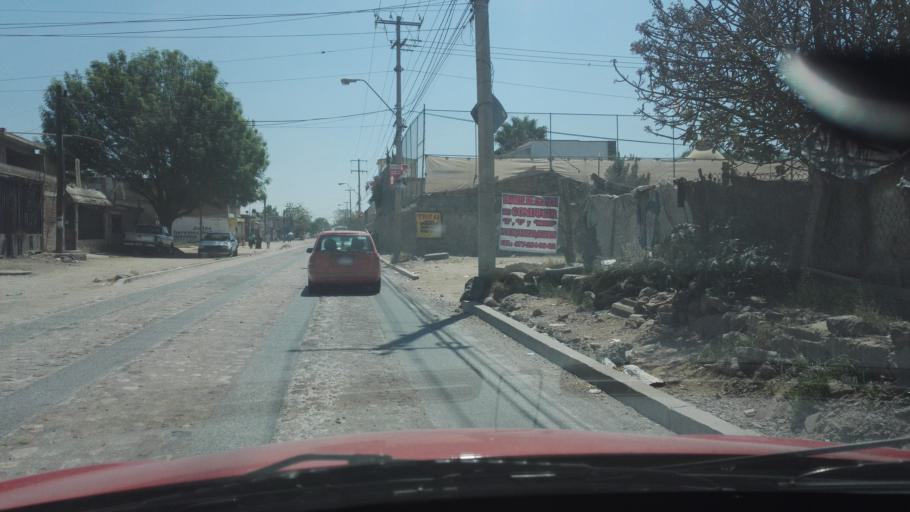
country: MX
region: Guanajuato
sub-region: Leon
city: Fraccionamiento Paraiso Real
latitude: 21.0961
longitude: -101.6024
